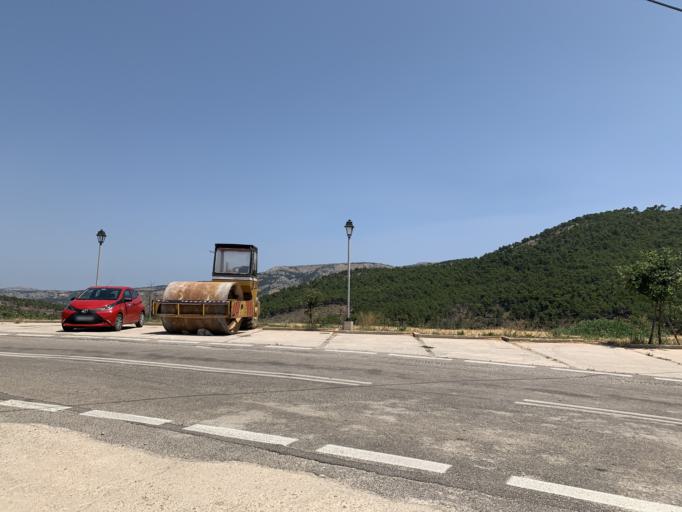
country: GR
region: North Aegean
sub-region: Chios
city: Chios
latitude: 38.3770
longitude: 26.0228
